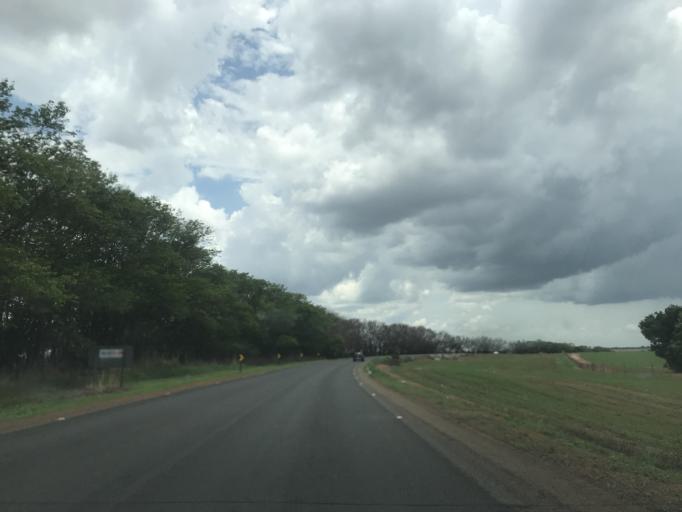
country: BR
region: Goias
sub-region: Vianopolis
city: Vianopolis
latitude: -16.8057
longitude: -48.5187
